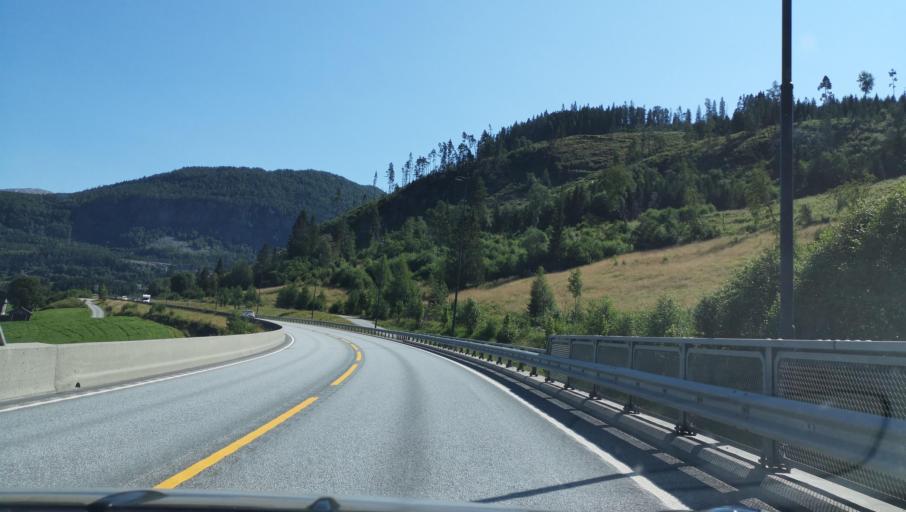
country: NO
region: Hordaland
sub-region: Voss
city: Voss
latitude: 60.6276
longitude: 6.5037
